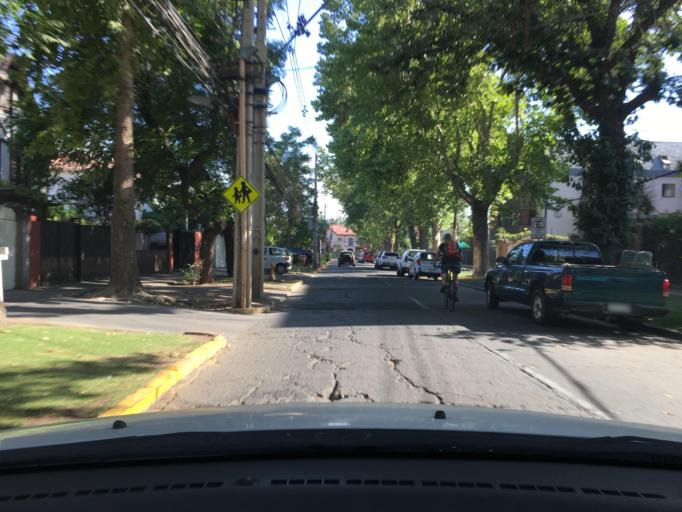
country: CL
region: Santiago Metropolitan
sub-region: Provincia de Santiago
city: Villa Presidente Frei, Nunoa, Santiago, Chile
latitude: -33.4580
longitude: -70.5922
